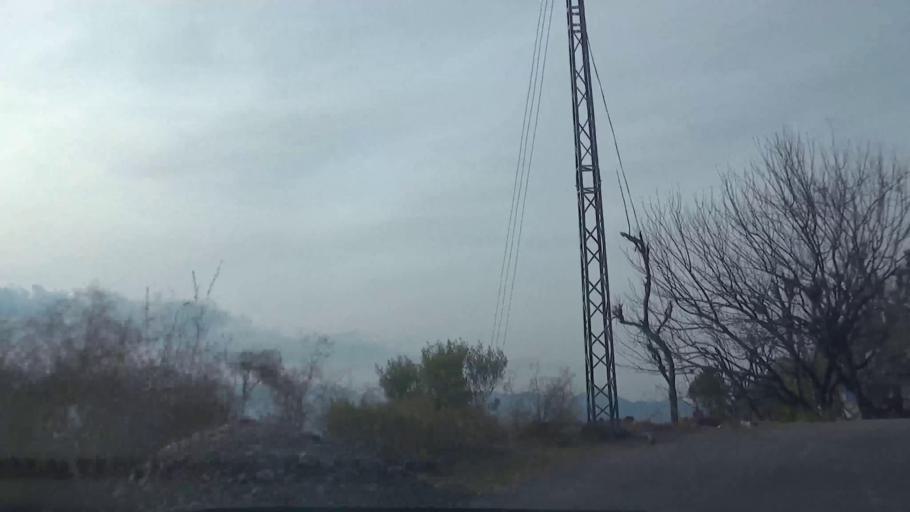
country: PK
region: Azad Kashmir
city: Muzaffarabad
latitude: 34.3630
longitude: 73.5059
